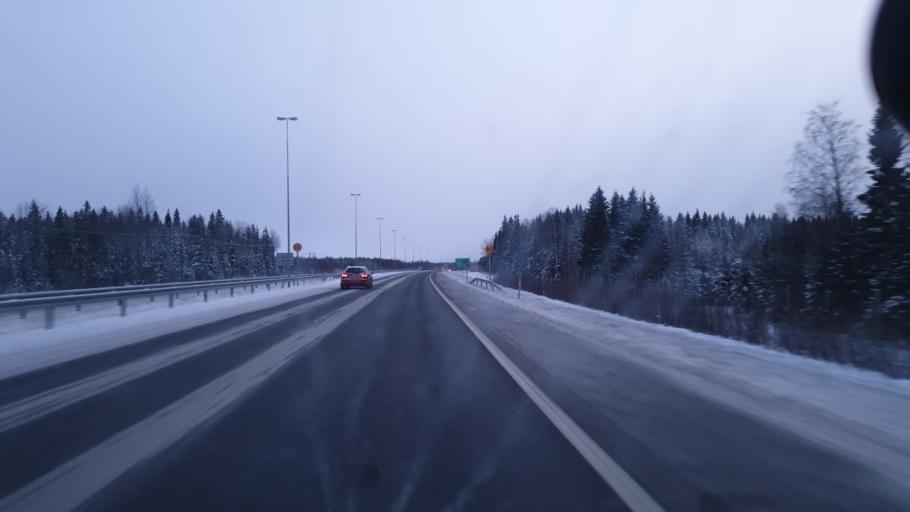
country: FI
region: Lapland
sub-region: Kemi-Tornio
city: Tornio
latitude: 65.8385
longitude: 24.2992
